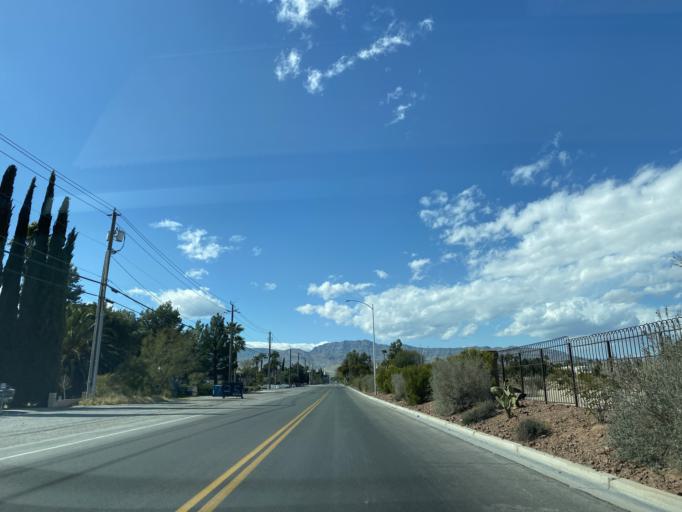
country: US
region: Nevada
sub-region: Clark County
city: Spring Valley
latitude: 36.2555
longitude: -115.2678
